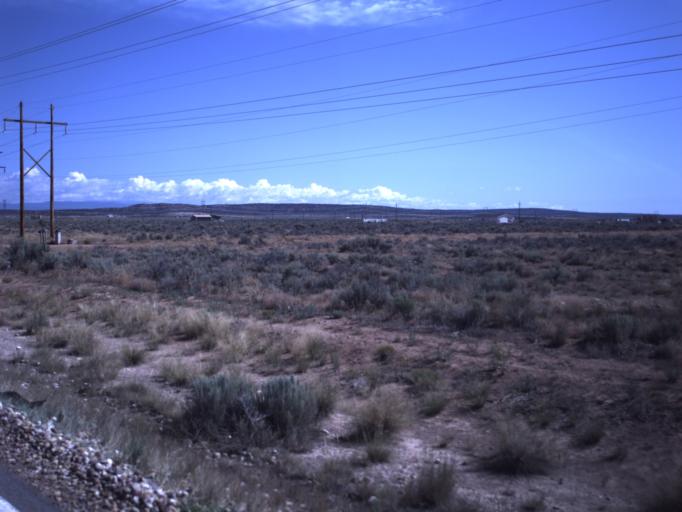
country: US
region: Utah
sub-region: Duchesne County
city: Duchesne
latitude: 40.2292
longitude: -110.3893
